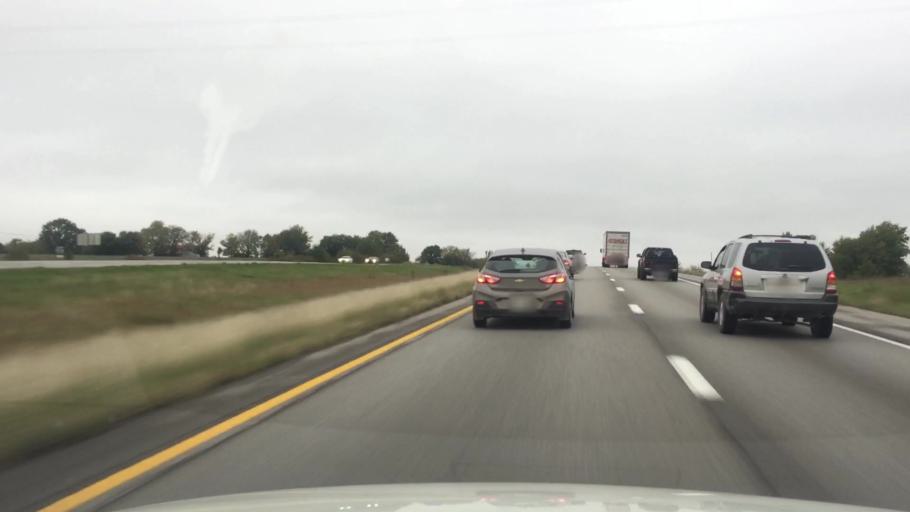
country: US
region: Missouri
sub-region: Jackson County
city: Oak Grove
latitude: 39.0169
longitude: -94.1512
